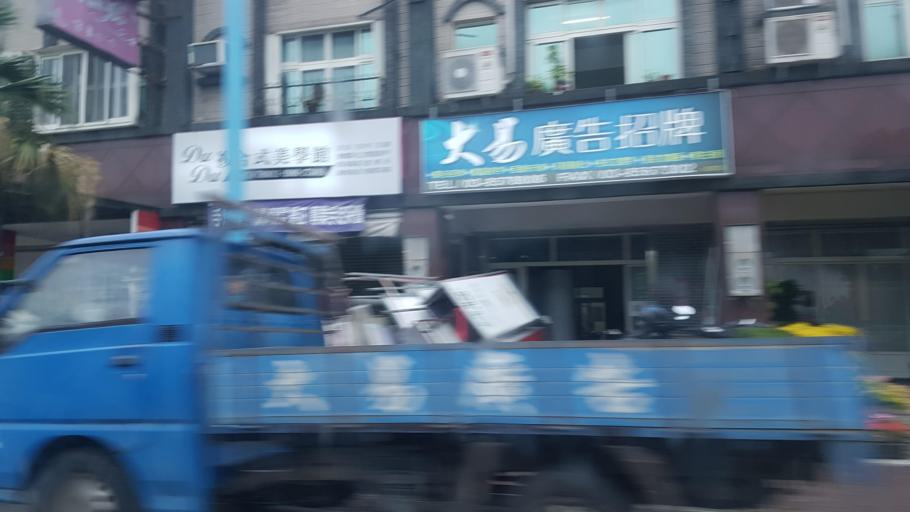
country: TW
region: Taiwan
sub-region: Hualien
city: Hualian
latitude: 23.9818
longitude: 121.5915
